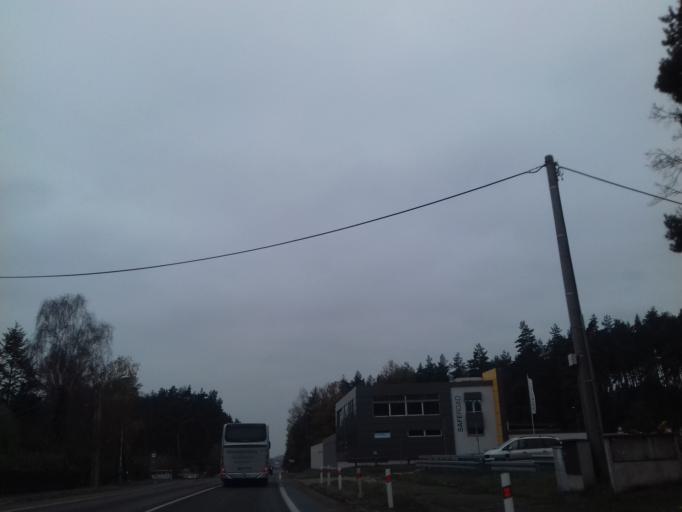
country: CZ
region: Plzensky
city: Vejprnice
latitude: 49.7065
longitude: 13.2776
